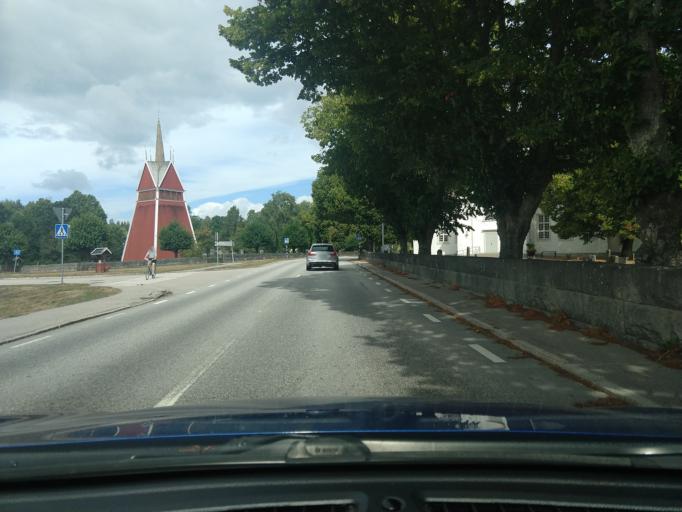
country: SE
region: Blekinge
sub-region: Ronneby Kommun
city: Brakne-Hoby
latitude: 56.3454
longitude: 15.1544
